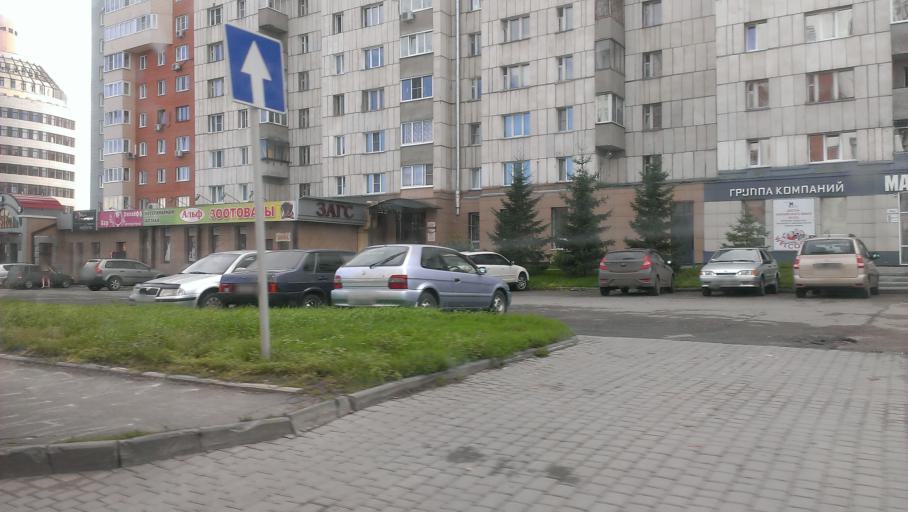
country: RU
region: Altai Krai
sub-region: Gorod Barnaulskiy
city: Barnaul
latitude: 53.3390
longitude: 83.7808
